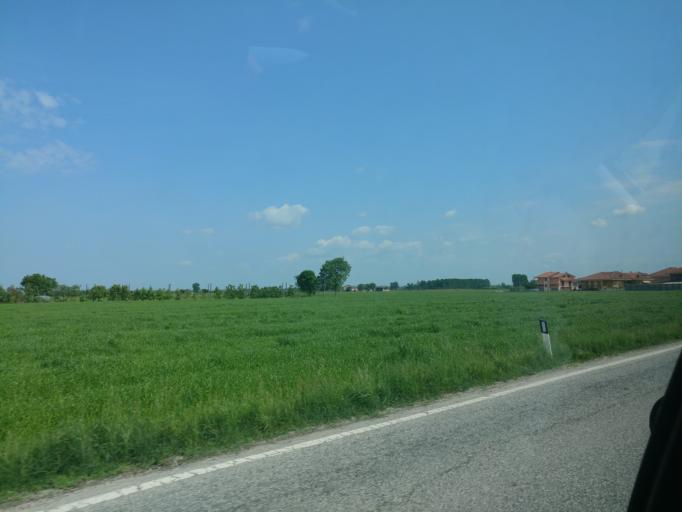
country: IT
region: Piedmont
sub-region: Provincia di Torino
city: Cavour
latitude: 44.7527
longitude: 7.4051
